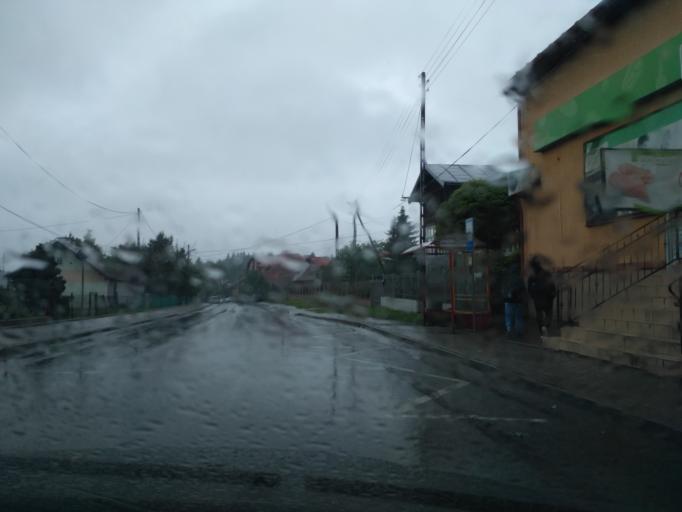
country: PL
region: Subcarpathian Voivodeship
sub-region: Powiat jasielski
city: Debowiec
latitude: 49.6821
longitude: 21.4597
